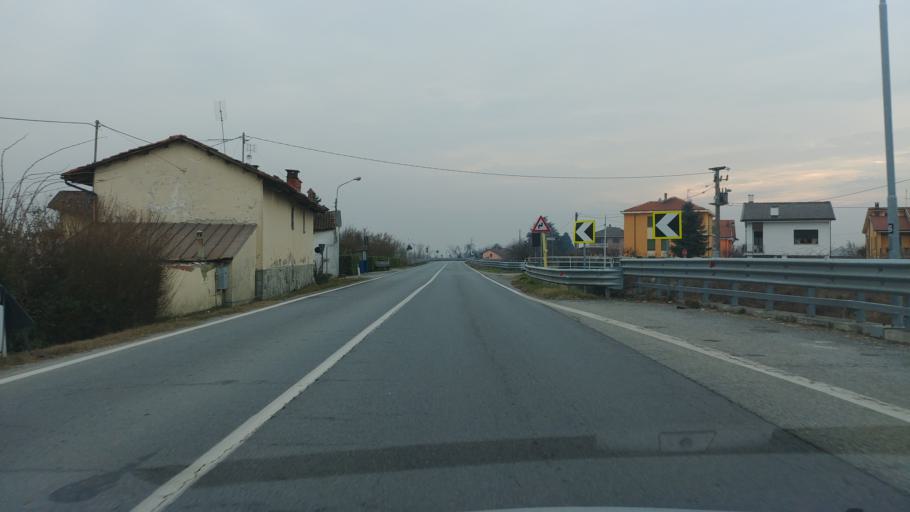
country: IT
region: Piedmont
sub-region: Provincia di Cuneo
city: Sant'Albano Stura
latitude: 44.5199
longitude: 7.6984
